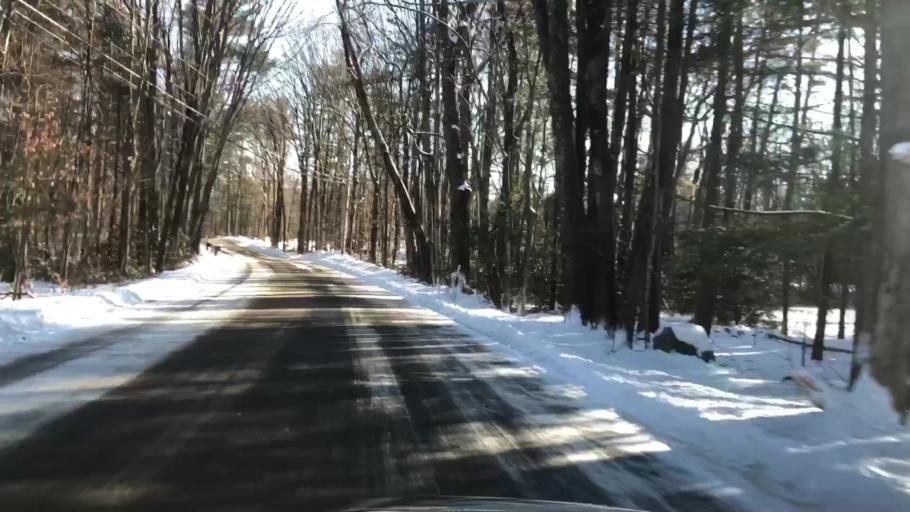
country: US
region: New Hampshire
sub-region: Hillsborough County
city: Wilton
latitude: 42.8167
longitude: -71.7225
